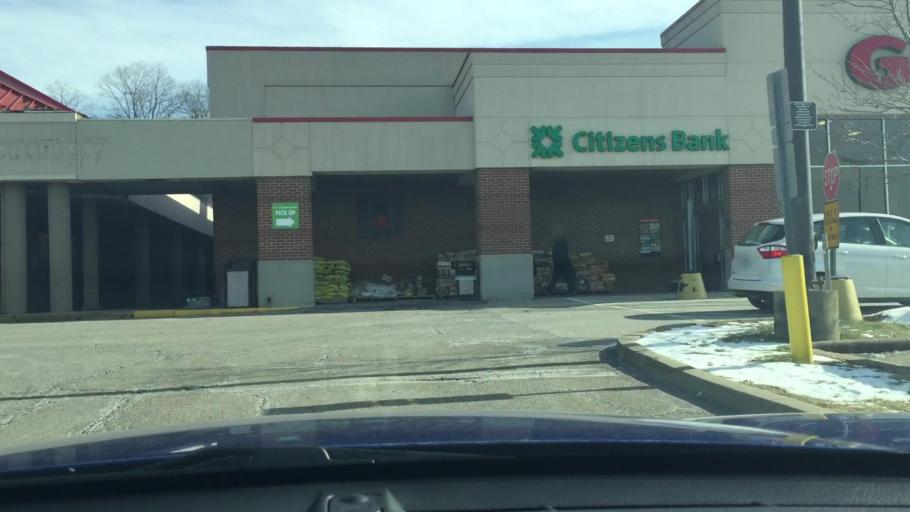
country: US
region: Pennsylvania
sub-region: Washington County
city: Thompsonville
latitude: 40.2697
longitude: -80.1271
